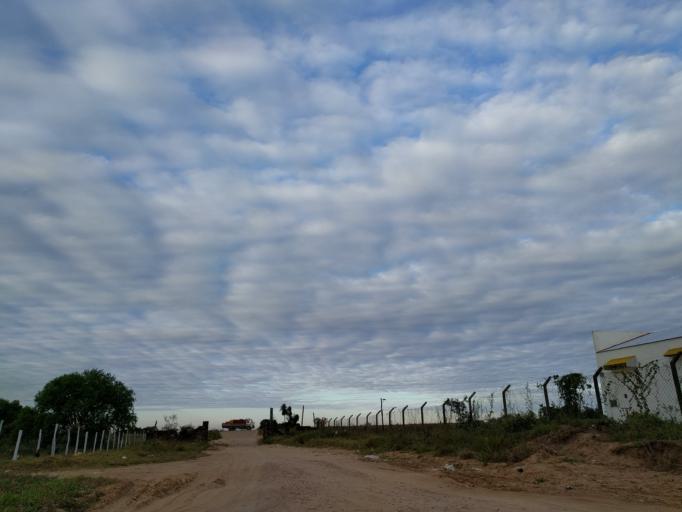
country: BO
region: Santa Cruz
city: Santa Rita
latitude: -17.8931
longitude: -63.2630
